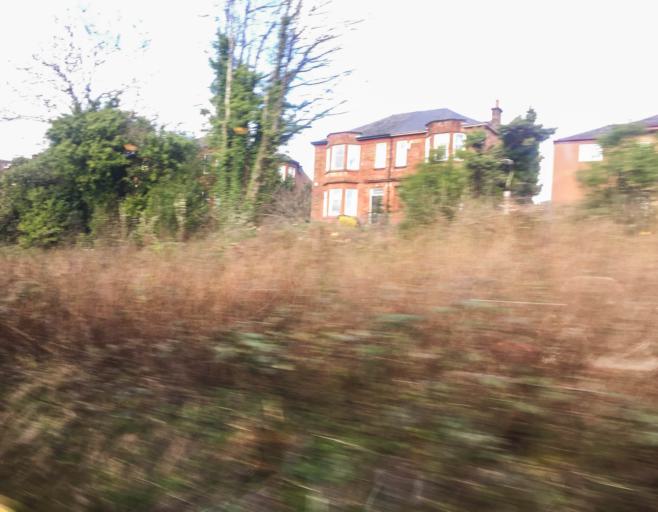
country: GB
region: Scotland
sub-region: West Dunbartonshire
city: Old Kilpatrick
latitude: 55.9250
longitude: -4.4540
